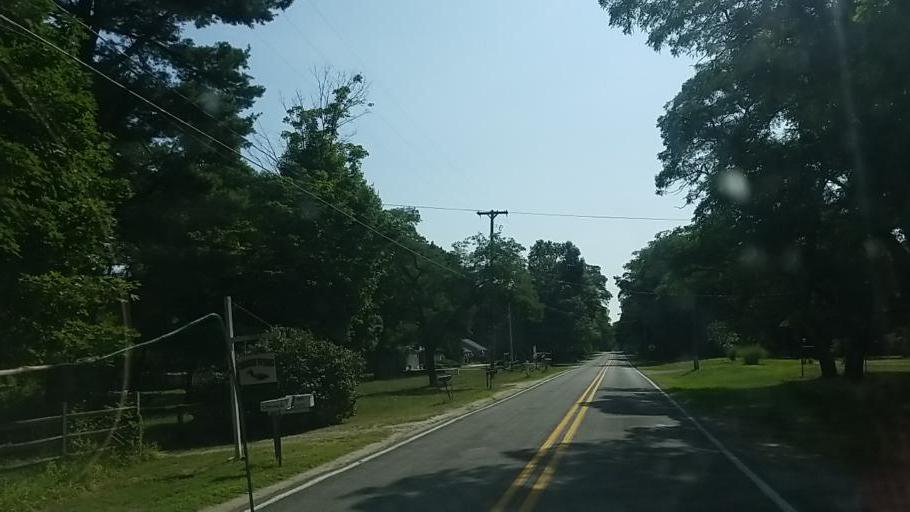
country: US
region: Michigan
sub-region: Muskegon County
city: Whitehall
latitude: 43.3710
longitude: -86.3801
